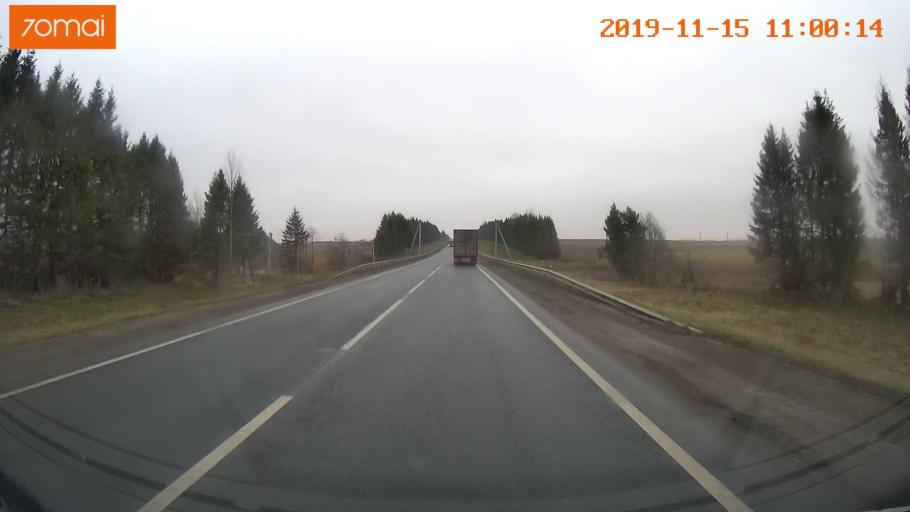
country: RU
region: Vologda
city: Chebsara
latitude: 59.1380
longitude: 38.8948
